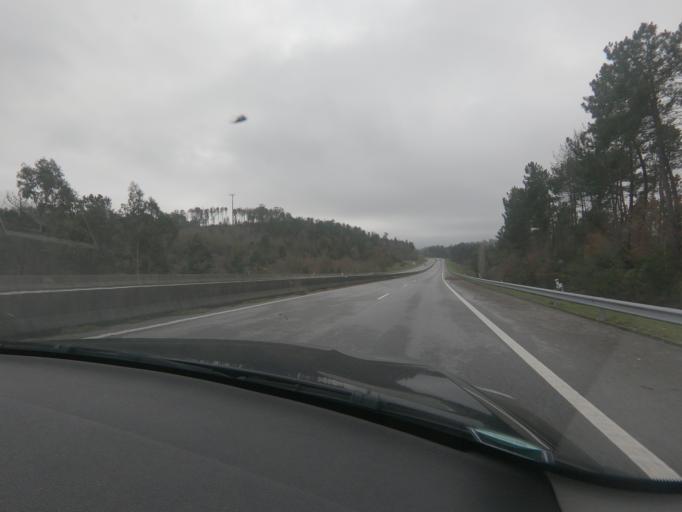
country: PT
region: Viseu
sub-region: Viseu
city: Abraveses
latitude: 40.6548
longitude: -7.9667
